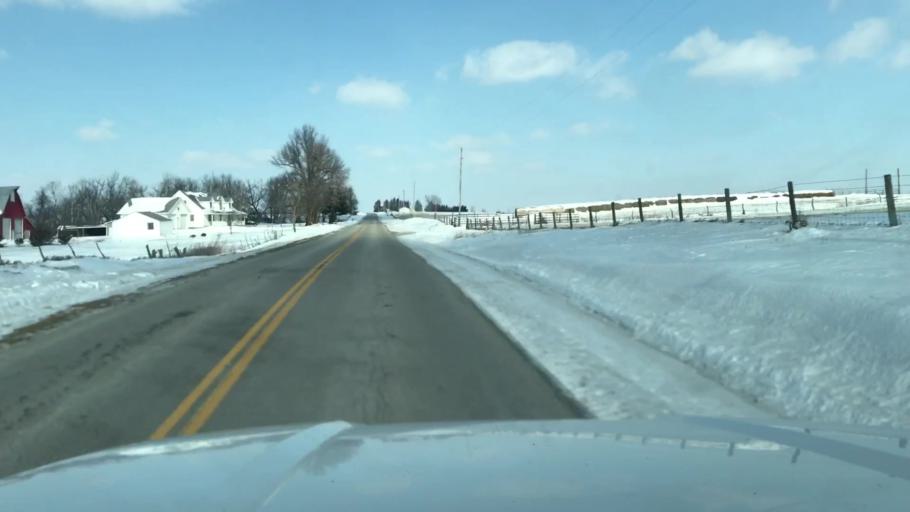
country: US
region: Missouri
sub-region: Nodaway County
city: Maryville
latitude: 40.3669
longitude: -94.7217
